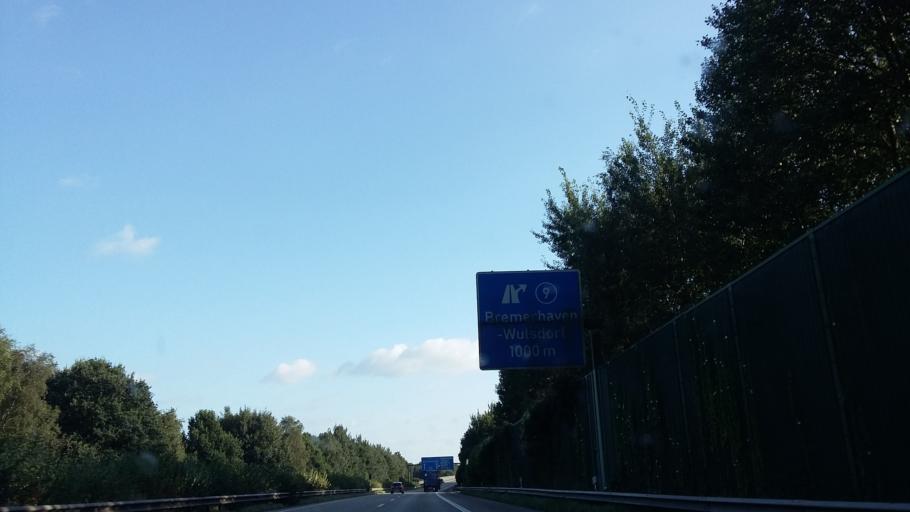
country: DE
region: Lower Saxony
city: Schiffdorf
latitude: 53.5072
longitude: 8.6290
